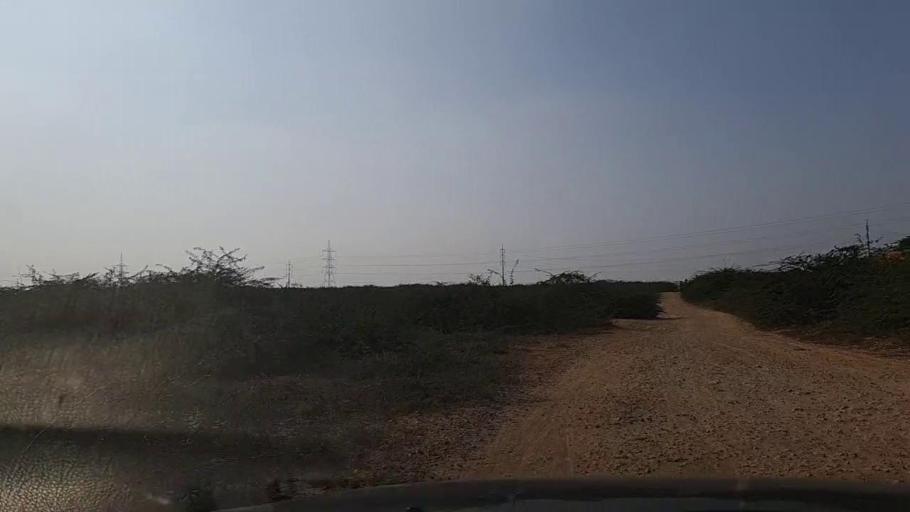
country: PK
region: Sindh
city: Gharo
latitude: 24.7523
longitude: 67.5429
